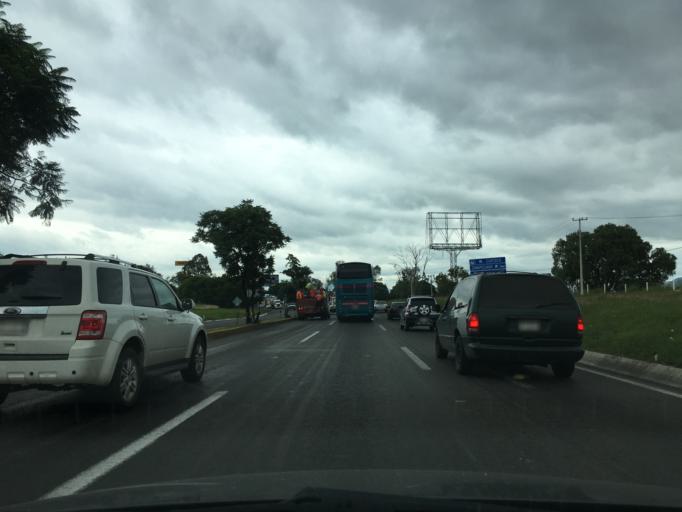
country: MX
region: Michoacan
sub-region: Tarimbaro
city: San Bernabe de las Canteras
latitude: 19.7666
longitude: -101.1601
